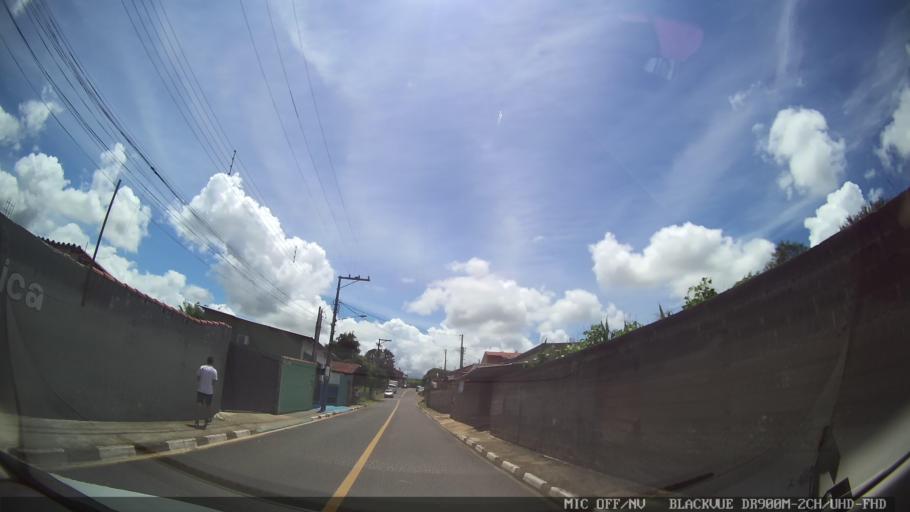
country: BR
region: Sao Paulo
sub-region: Amparo
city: Amparo
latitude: -22.8149
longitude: -46.6928
